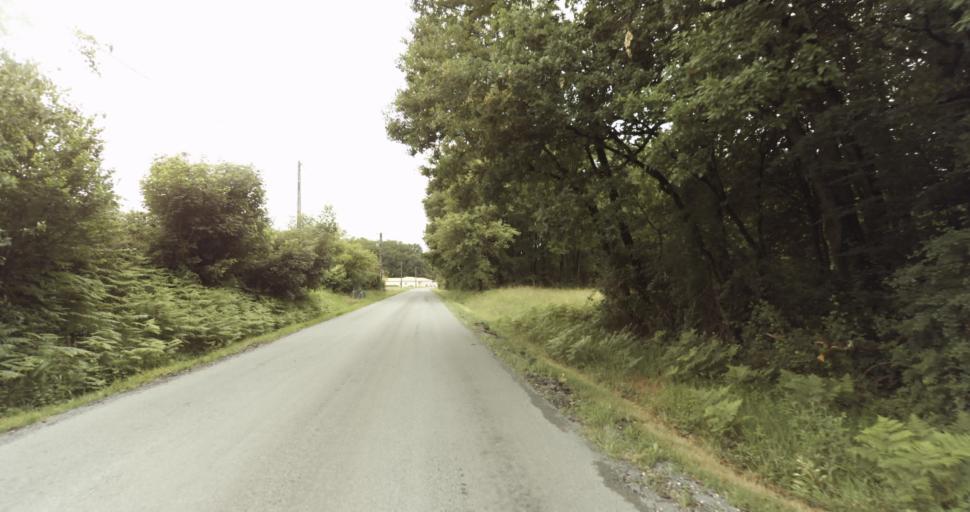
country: FR
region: Aquitaine
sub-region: Departement de la Dordogne
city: Beaumont-du-Perigord
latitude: 44.7084
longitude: 0.8149
